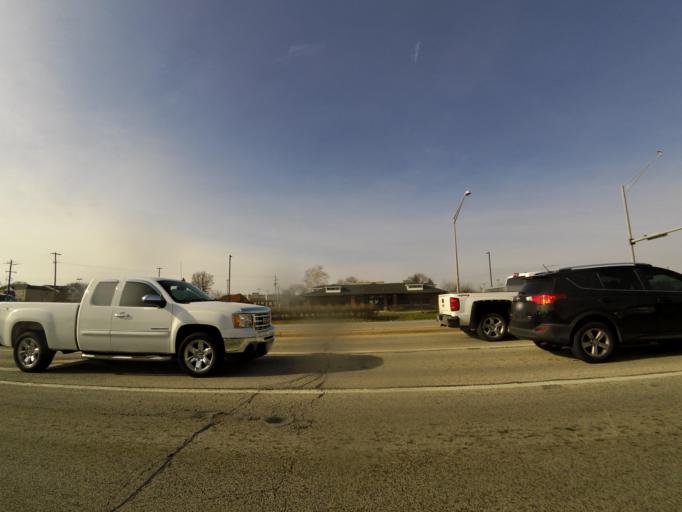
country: US
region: Illinois
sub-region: Macon County
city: Forsyth
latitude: 39.9172
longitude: -88.9553
